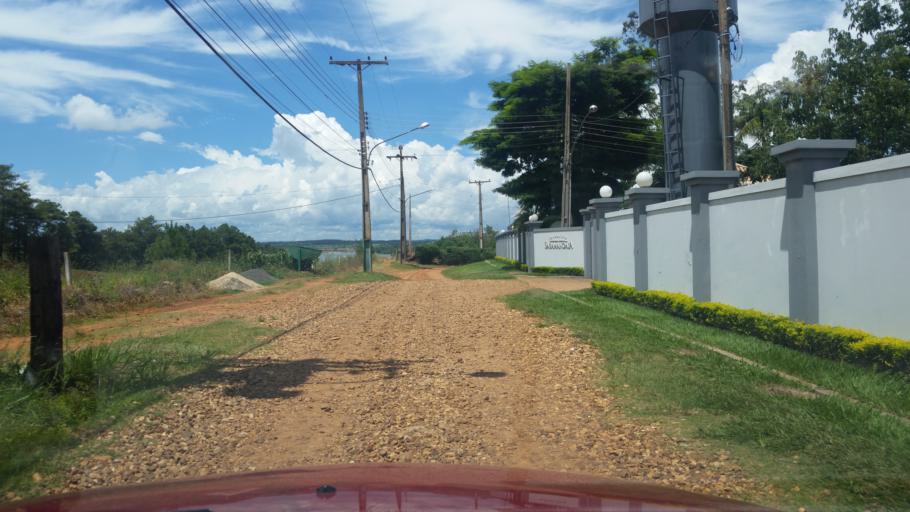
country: BR
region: Sao Paulo
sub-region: Itai
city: Itai
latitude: -23.2758
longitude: -49.0197
